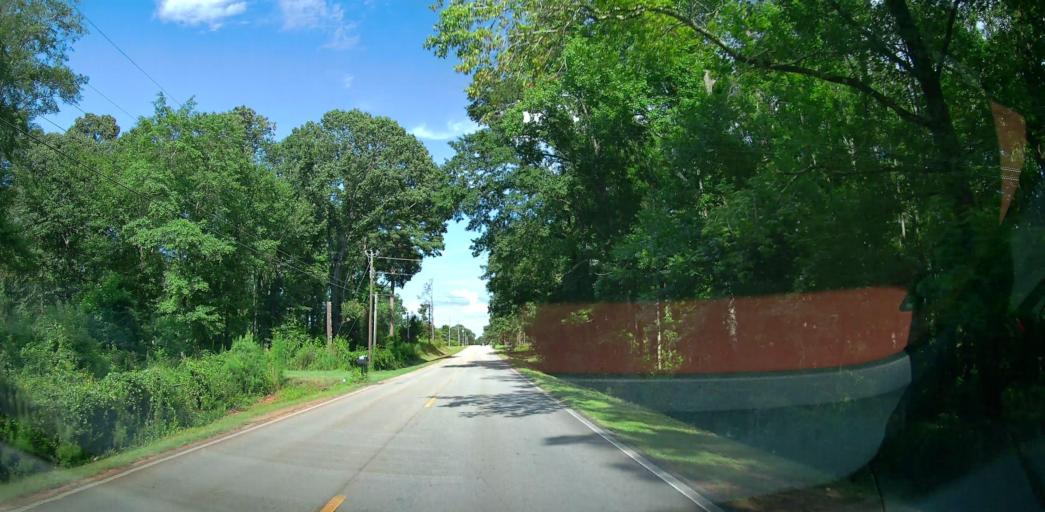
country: US
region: Georgia
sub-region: Houston County
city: Robins Air Force Base
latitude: 32.5383
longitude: -83.6508
